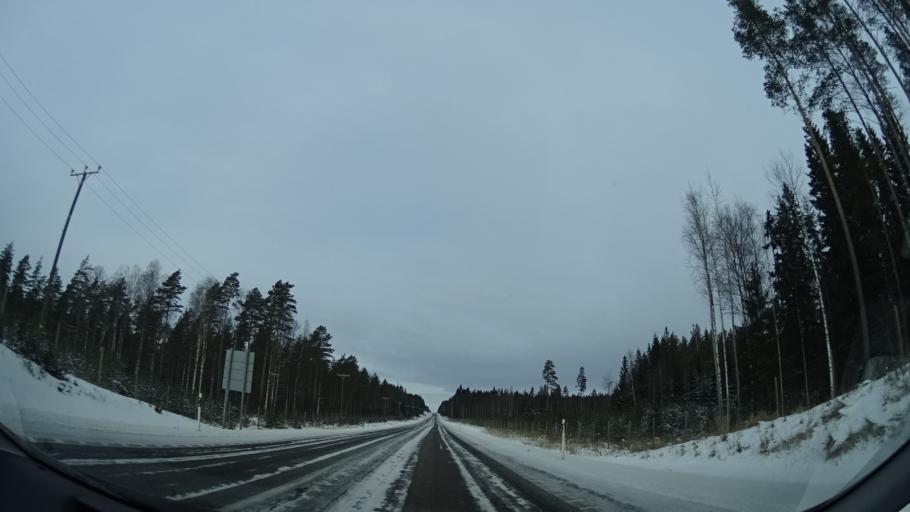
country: FI
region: Uusimaa
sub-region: Helsinki
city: Kaerkoelae
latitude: 60.6487
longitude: 23.8682
